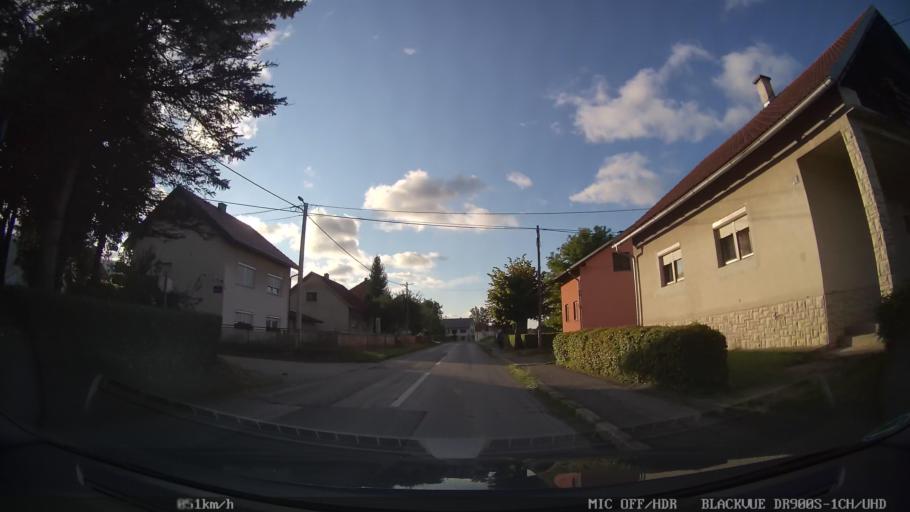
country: HR
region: Karlovacka
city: Plaski
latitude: 45.0772
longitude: 15.3661
